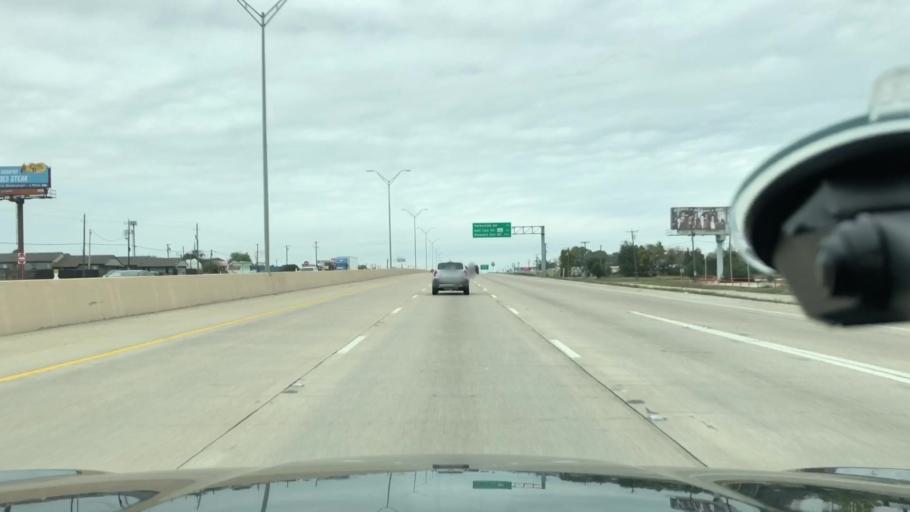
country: US
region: Texas
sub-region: Dallas County
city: Glenn Heights
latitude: 32.5656
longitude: -96.8224
